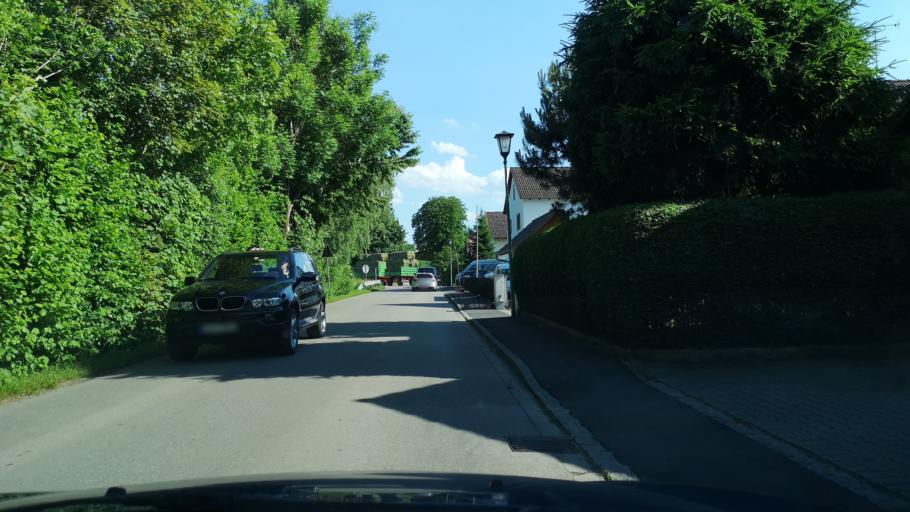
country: DE
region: Bavaria
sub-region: Upper Bavaria
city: Eichenried
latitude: 48.2444
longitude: 11.7806
